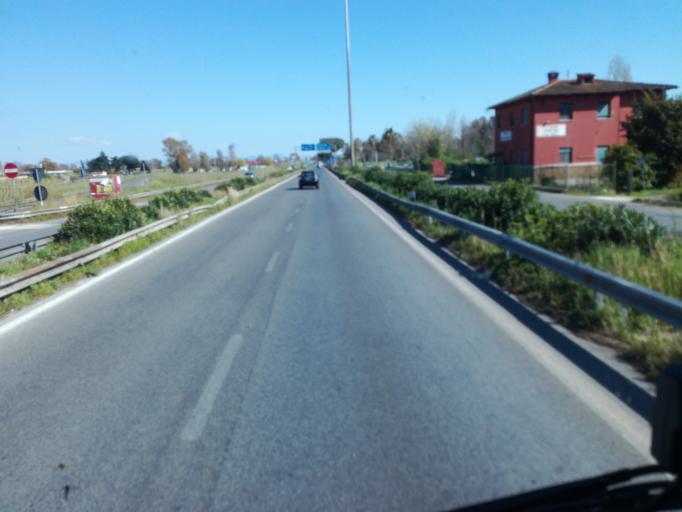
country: IT
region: Latium
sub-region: Provincia di Latina
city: Borgo Podgora
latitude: 41.4873
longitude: 12.8492
